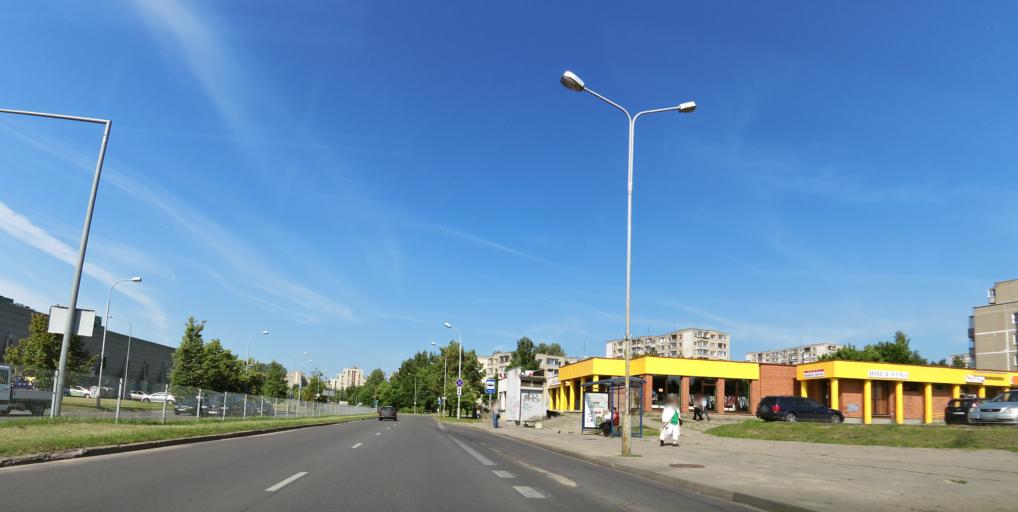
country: LT
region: Vilnius County
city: Justiniskes
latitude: 54.7164
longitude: 25.2303
